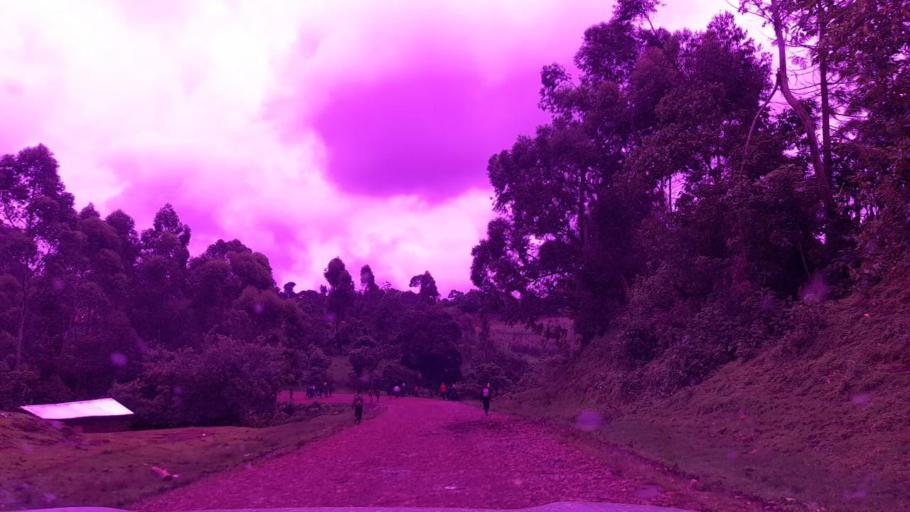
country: ET
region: Southern Nations, Nationalities, and People's Region
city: Tippi
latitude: 7.5901
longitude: 35.7660
